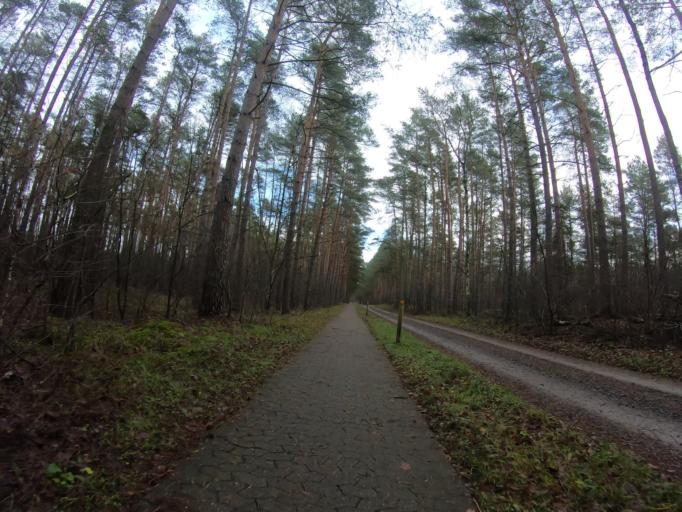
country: DE
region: Lower Saxony
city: Wagenhoff
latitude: 52.4907
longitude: 10.4960
